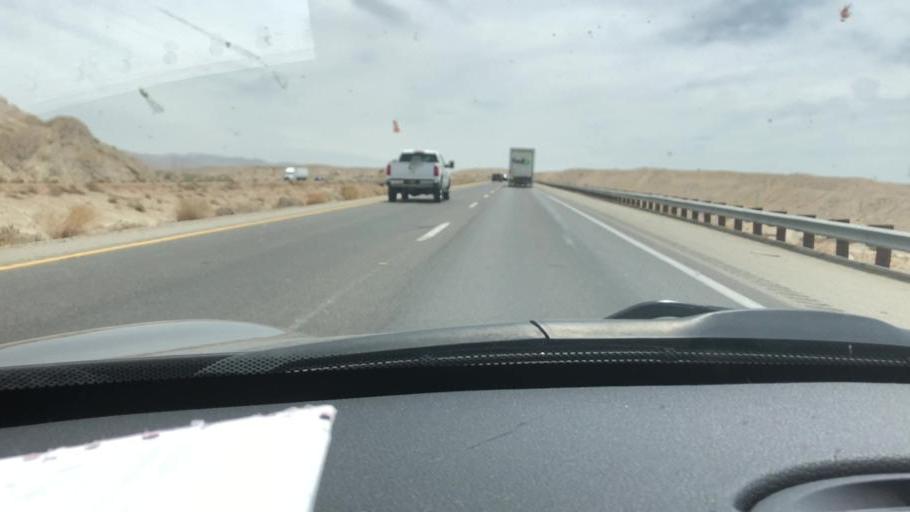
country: US
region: California
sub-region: Riverside County
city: Thermal
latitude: 33.6991
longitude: -116.1099
